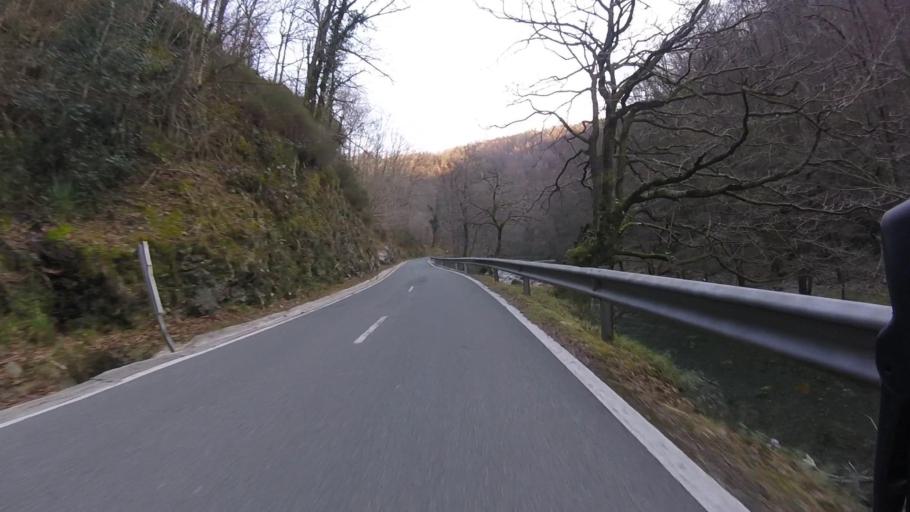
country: ES
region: Navarre
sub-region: Provincia de Navarra
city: Arano
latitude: 43.2099
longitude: -1.8693
